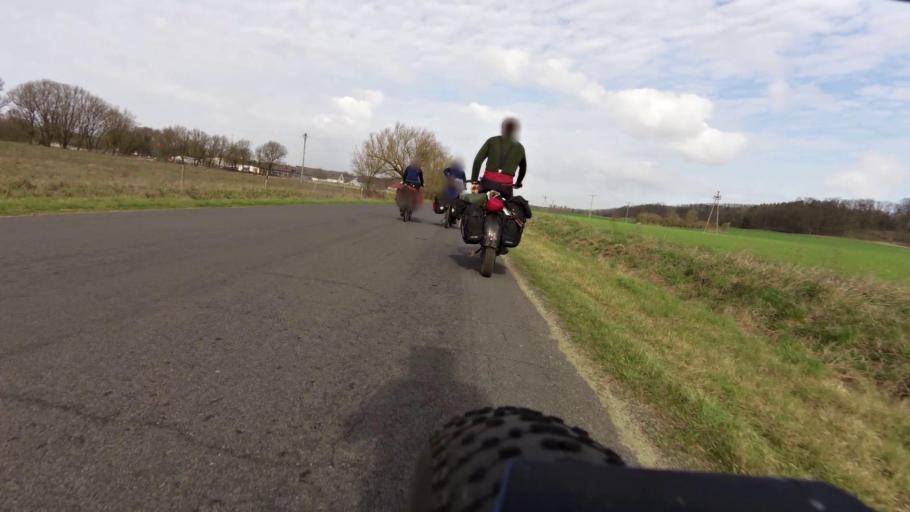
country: DE
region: Brandenburg
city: Brieskow-Finkenheerd
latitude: 52.2998
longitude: 14.6005
